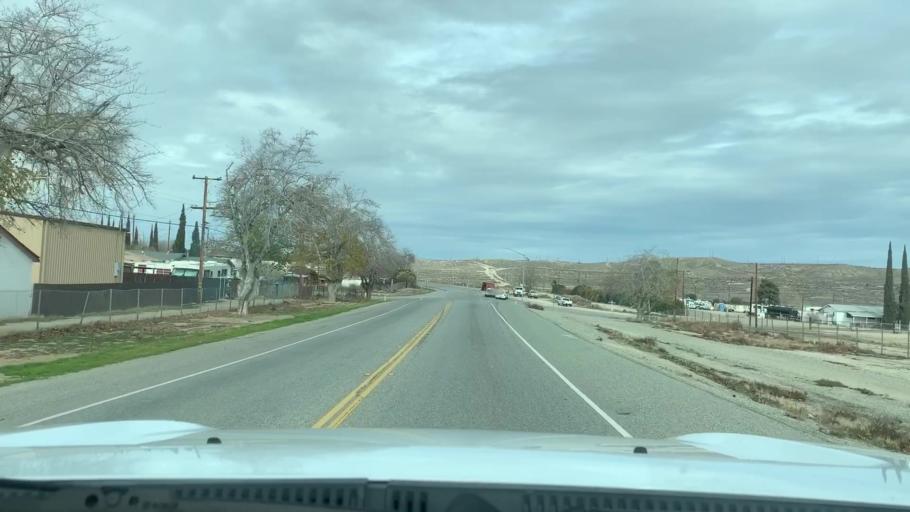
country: US
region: California
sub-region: Kern County
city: Ford City
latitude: 35.1534
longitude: -119.4479
